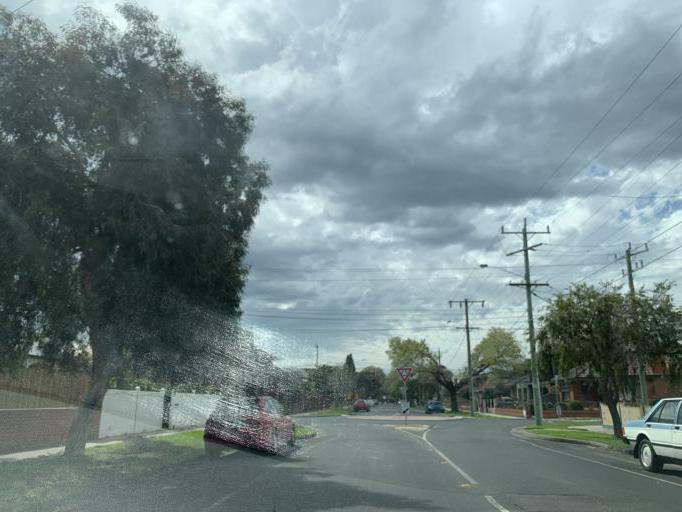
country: AU
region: Victoria
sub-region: Moreland
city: Coburg
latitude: -37.7543
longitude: 144.9662
